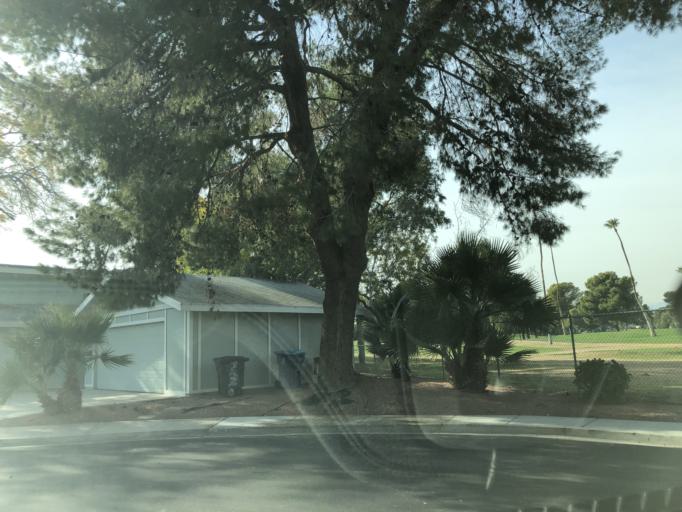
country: US
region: Nevada
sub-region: Clark County
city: Winchester
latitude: 36.1280
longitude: -115.1214
